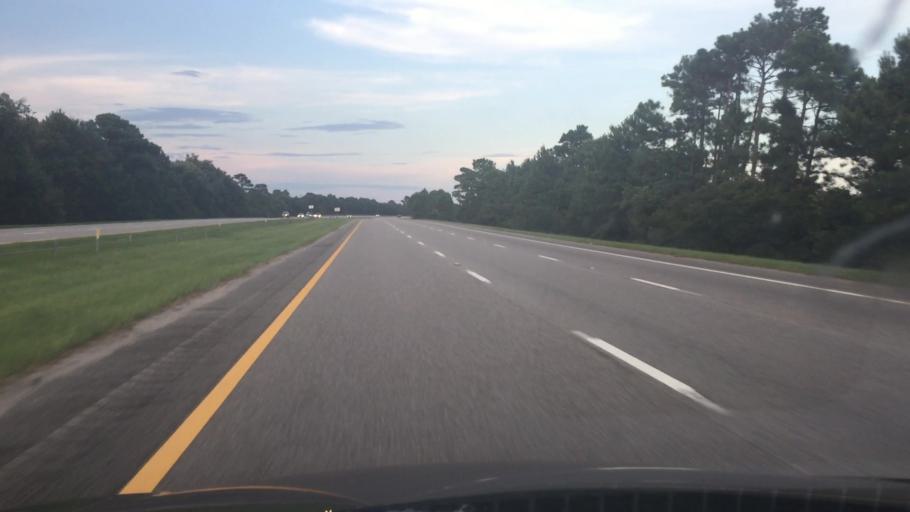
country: US
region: South Carolina
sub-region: Horry County
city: Forestbrook
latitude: 33.7491
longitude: -78.9040
